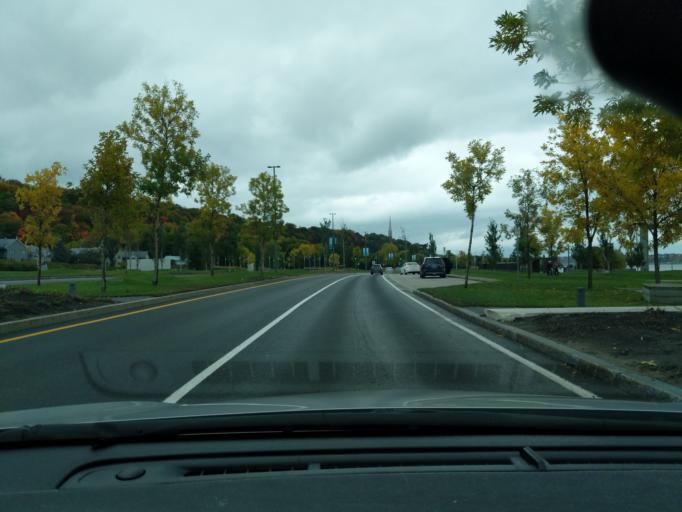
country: CA
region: Quebec
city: Quebec
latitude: 46.7690
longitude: -71.2546
